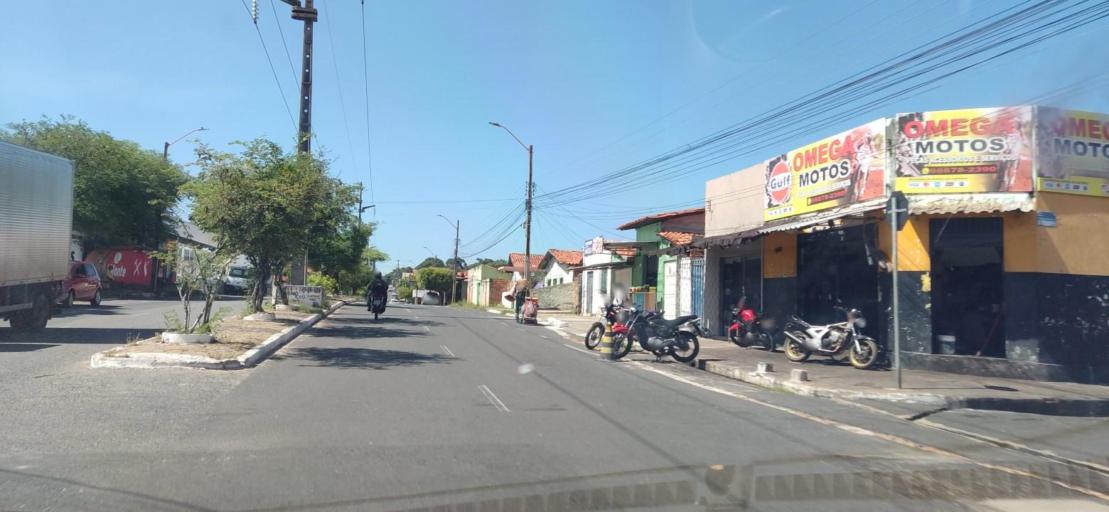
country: BR
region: Piaui
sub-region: Teresina
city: Teresina
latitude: -5.1182
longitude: -42.8104
